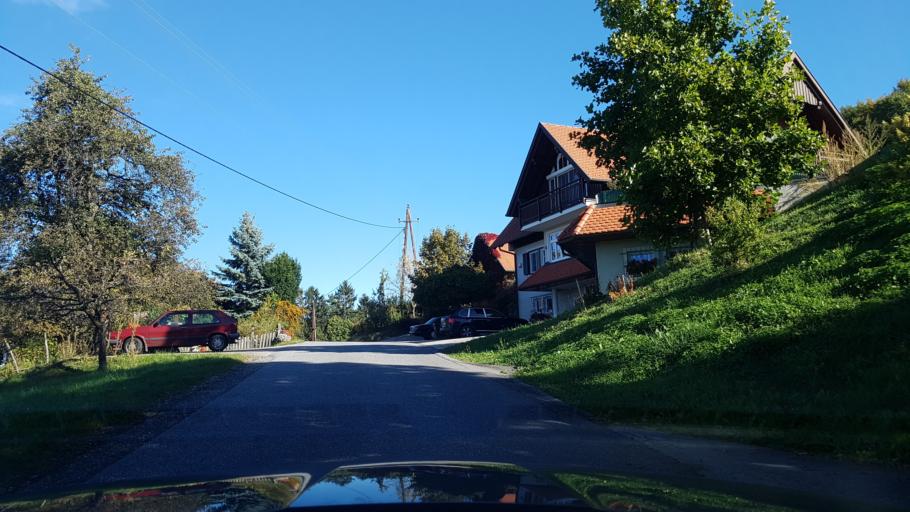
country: AT
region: Styria
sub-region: Politischer Bezirk Leibnitz
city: Kitzeck im Sausal
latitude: 46.7836
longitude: 15.4177
